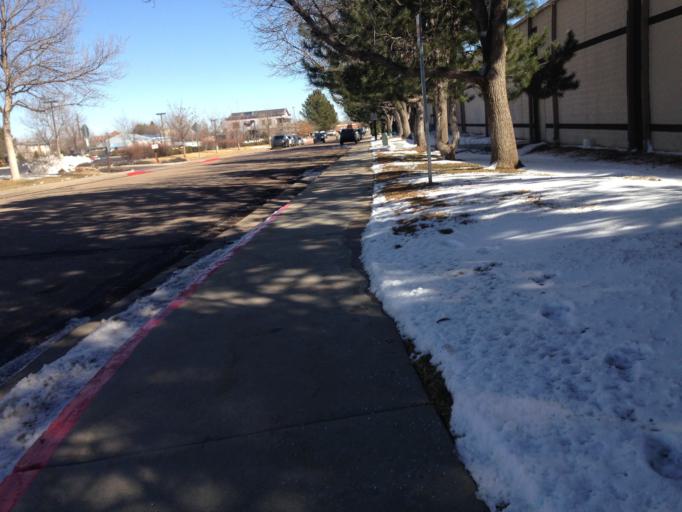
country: US
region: Colorado
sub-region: Boulder County
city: Lafayette
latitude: 39.9892
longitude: -105.0942
